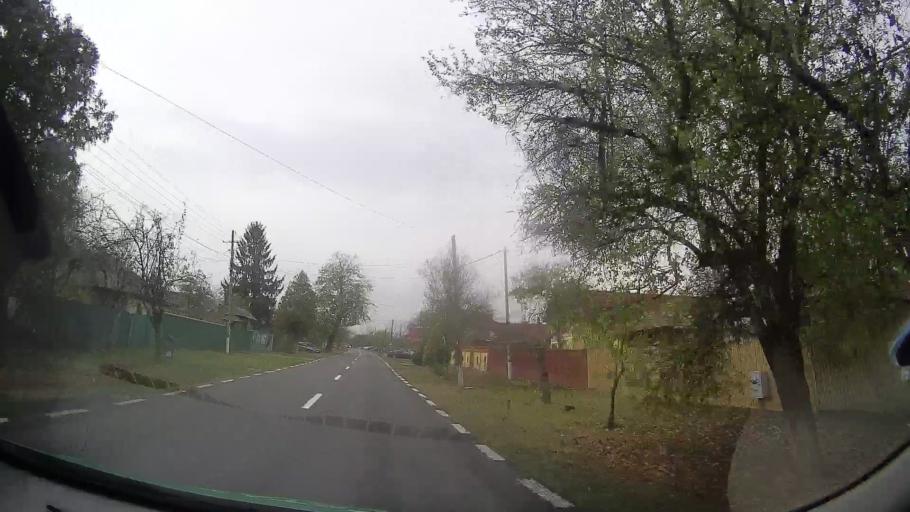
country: RO
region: Ilfov
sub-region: Comuna Gruiu
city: Lipia
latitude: 44.7147
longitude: 26.2569
